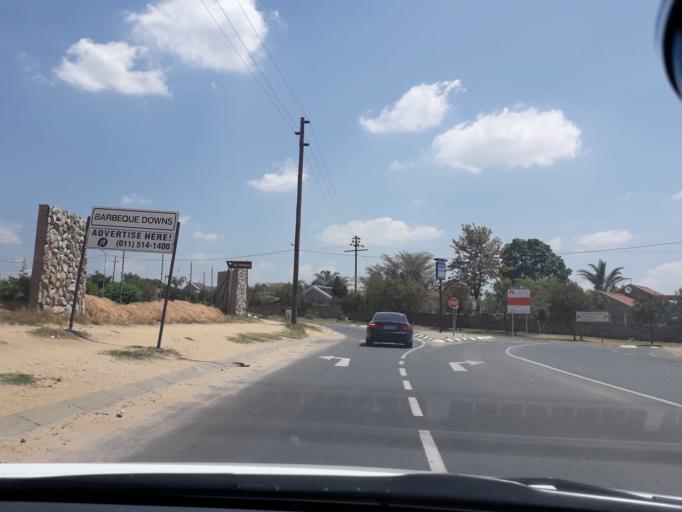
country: ZA
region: Gauteng
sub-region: City of Johannesburg Metropolitan Municipality
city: Midrand
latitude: -26.0094
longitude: 28.0782
